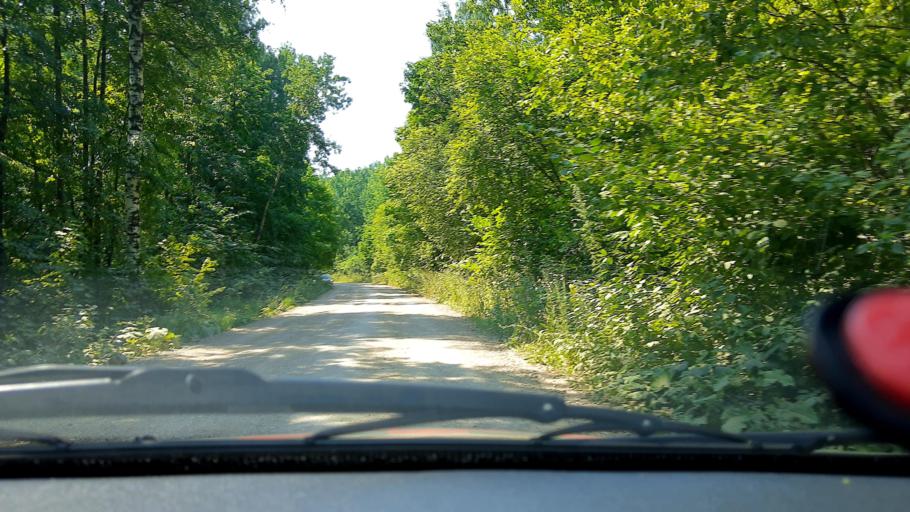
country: RU
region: Bashkortostan
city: Karmaskaly
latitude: 54.3900
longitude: 55.8971
